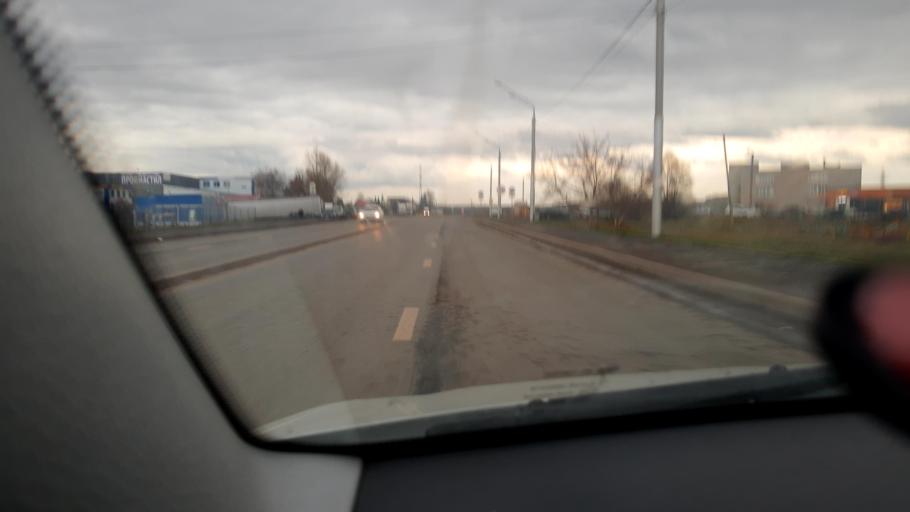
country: RU
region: Bashkortostan
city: Iglino
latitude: 54.7570
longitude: 56.2477
